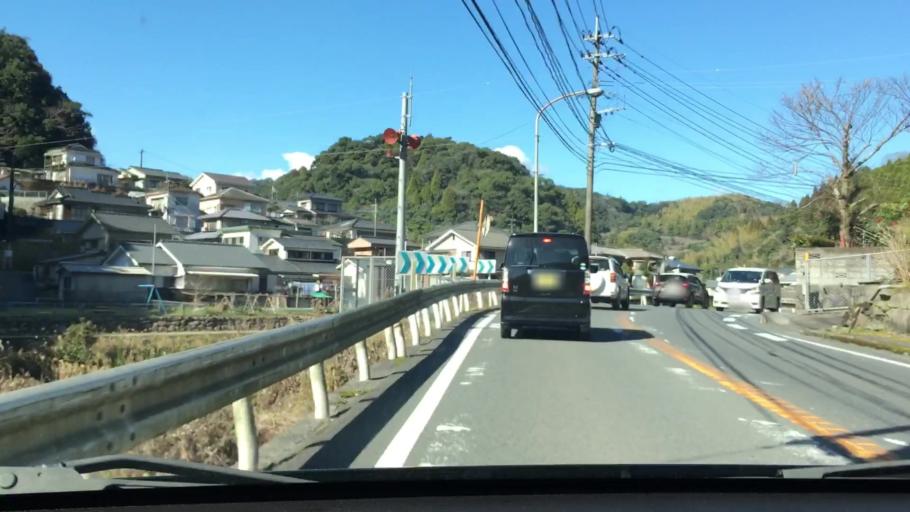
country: JP
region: Kagoshima
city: Kagoshima-shi
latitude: 31.6497
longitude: 130.5129
